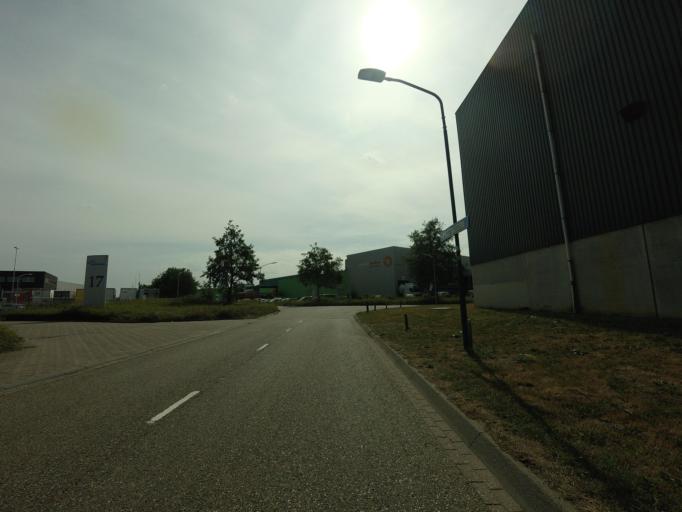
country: NL
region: North Brabant
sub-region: Gemeente Helmond
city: Helmond
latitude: 51.4452
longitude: 5.6959
